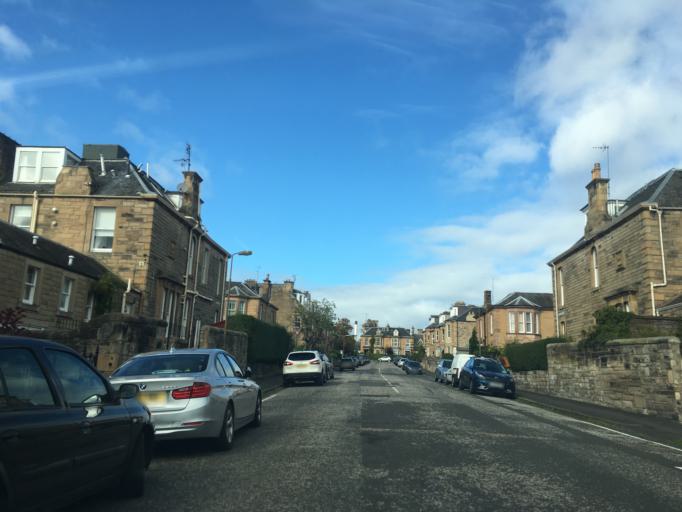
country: GB
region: Scotland
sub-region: Edinburgh
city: Edinburgh
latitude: 55.9351
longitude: -3.1667
